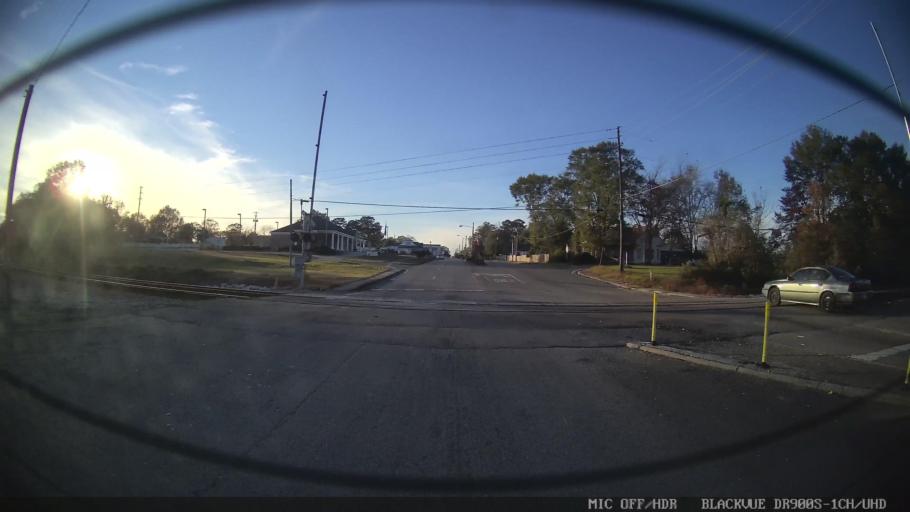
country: US
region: Mississippi
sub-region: Lamar County
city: Lumberton
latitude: 30.9997
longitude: -89.4477
